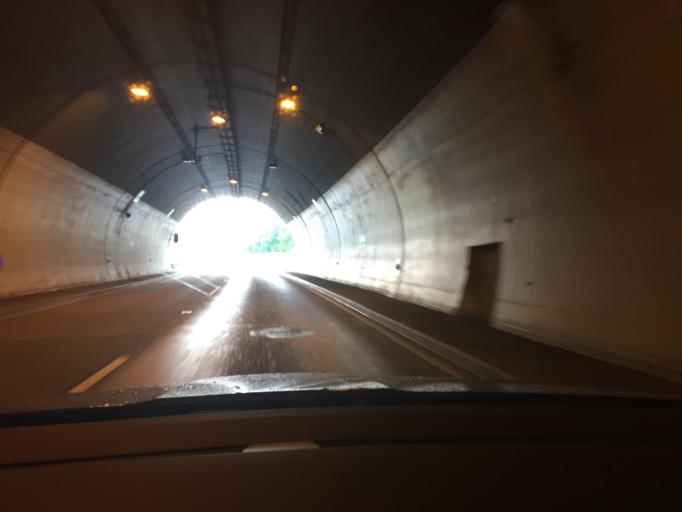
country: CZ
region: Ustecky
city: Libouchec
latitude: 50.7471
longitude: 14.0053
